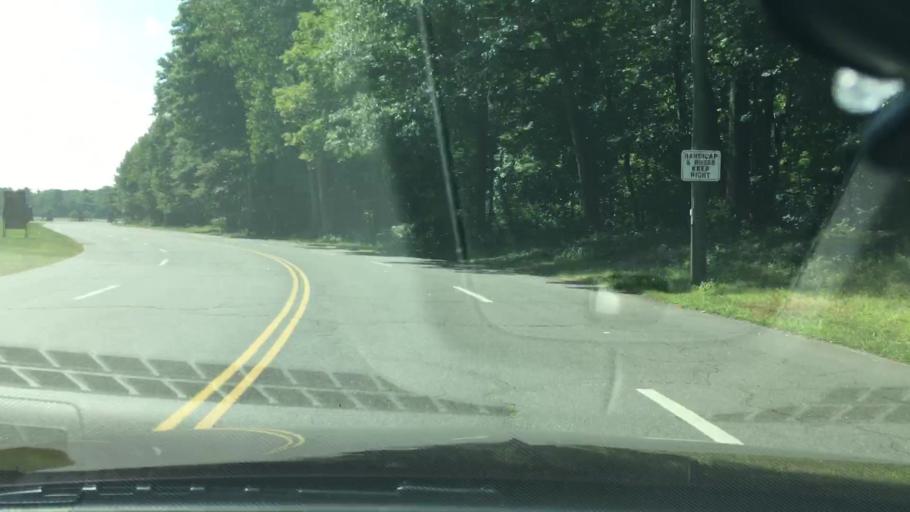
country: US
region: Connecticut
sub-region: Hartford County
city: Bristol
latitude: 41.6454
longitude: -72.9199
